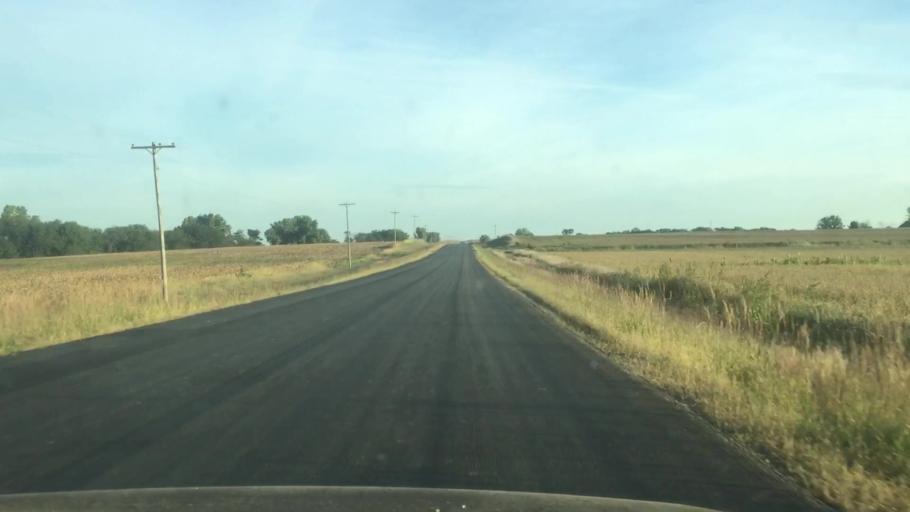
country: US
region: Kansas
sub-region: Marshall County
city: Marysville
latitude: 39.8766
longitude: -96.6009
